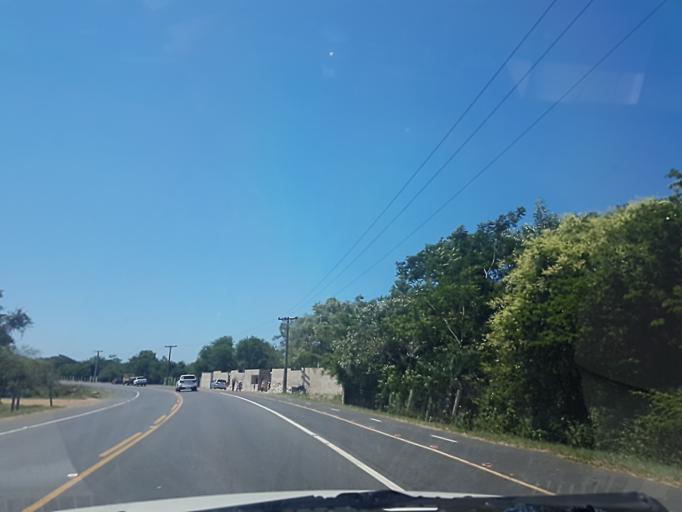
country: PY
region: Cordillera
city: San Bernardino
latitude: -25.2573
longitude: -57.3206
